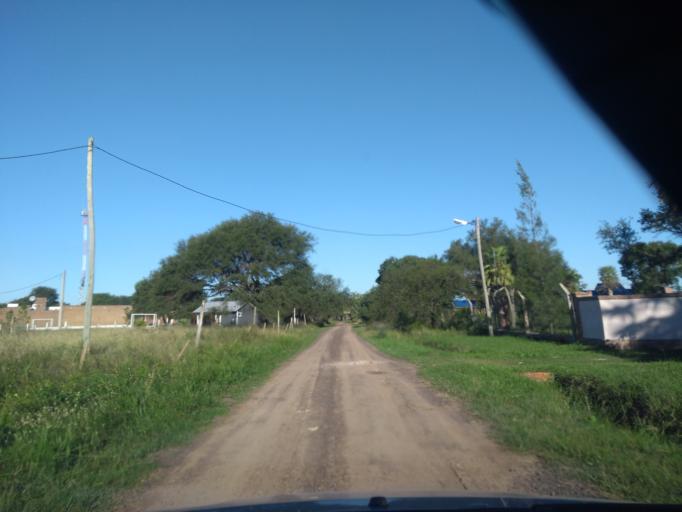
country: AR
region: Chaco
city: Barranqueras
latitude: -27.4406
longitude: -58.9059
